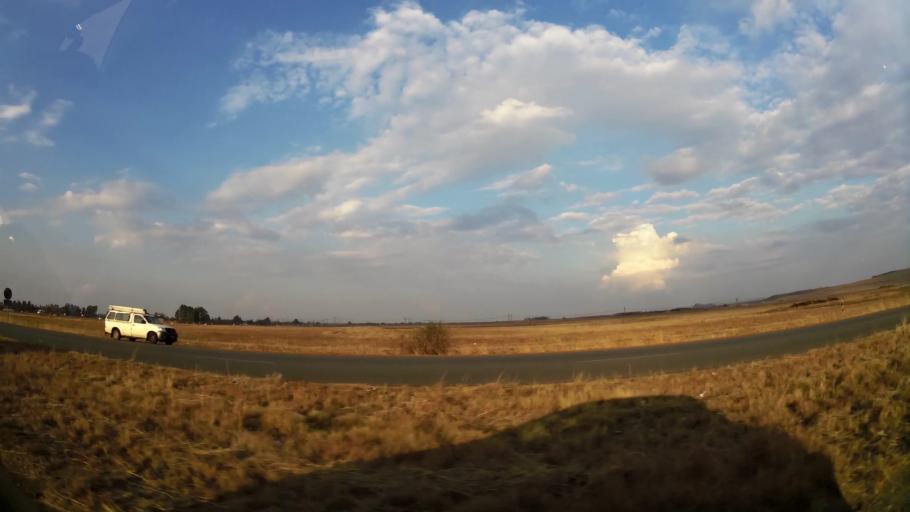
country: ZA
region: Gauteng
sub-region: Sedibeng District Municipality
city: Vanderbijlpark
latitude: -26.6211
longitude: 27.8120
